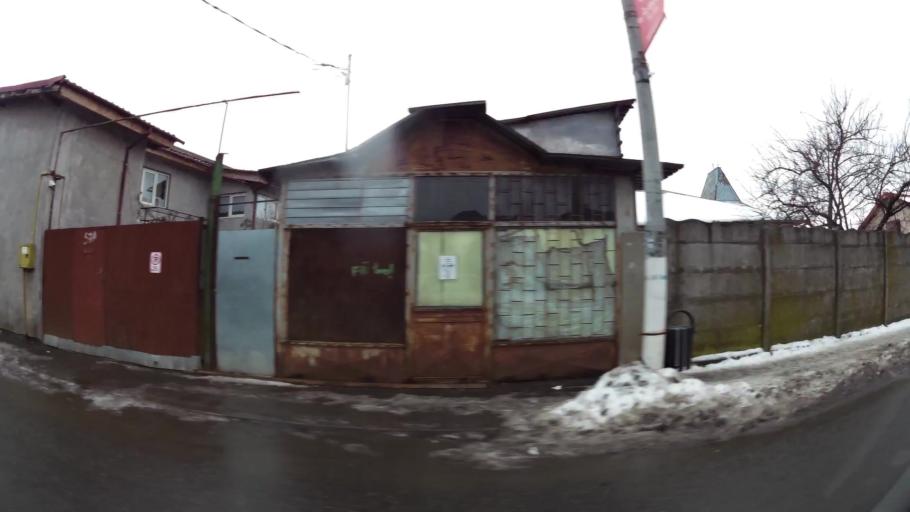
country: RO
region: Ilfov
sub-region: Comuna Pantelimon
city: Pantelimon
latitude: 44.4527
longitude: 26.2028
